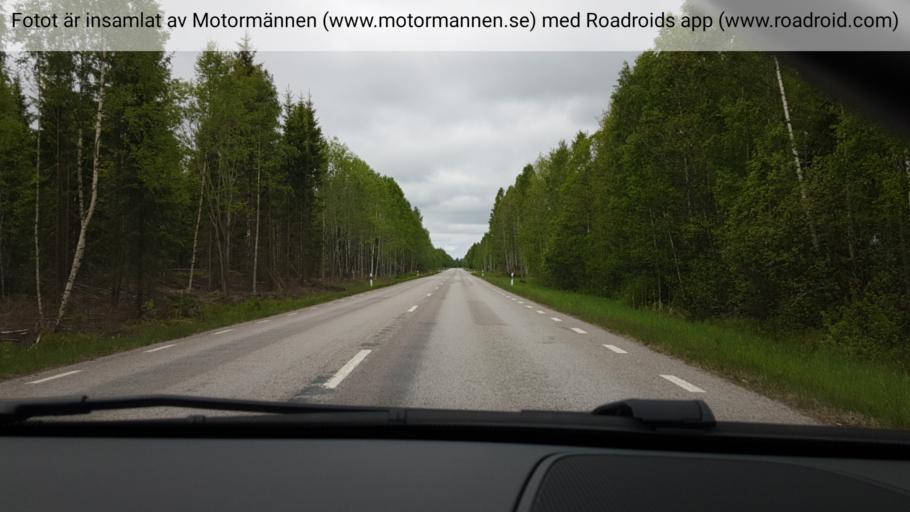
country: SE
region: Uppsala
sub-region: Tierps Kommun
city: Tierp
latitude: 60.3595
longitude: 17.3592
